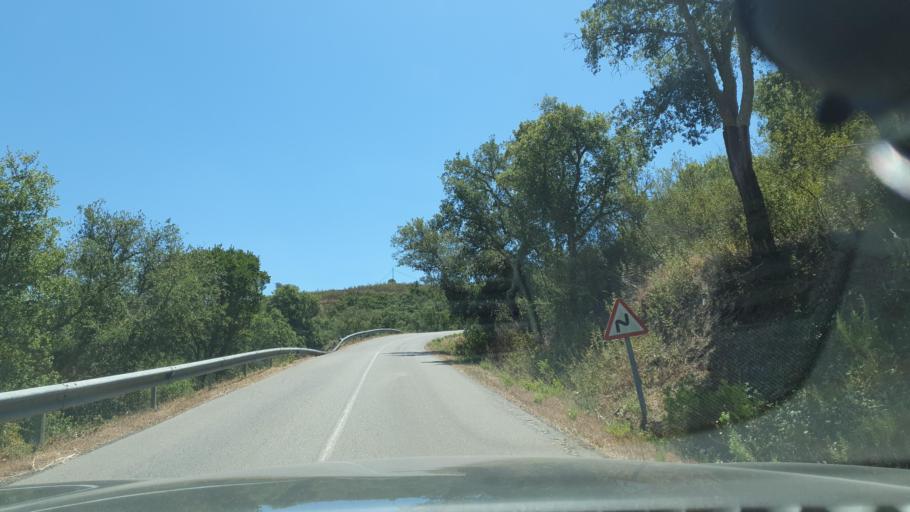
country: PT
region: Beja
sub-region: Odemira
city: Odemira
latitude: 37.5563
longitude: -8.4463
